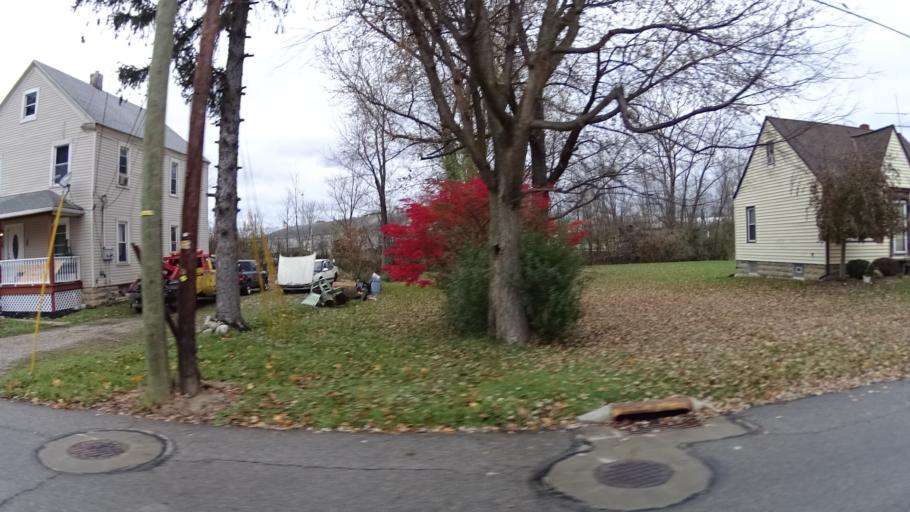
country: US
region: Ohio
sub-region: Lorain County
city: Elyria
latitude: 41.3515
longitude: -82.1232
